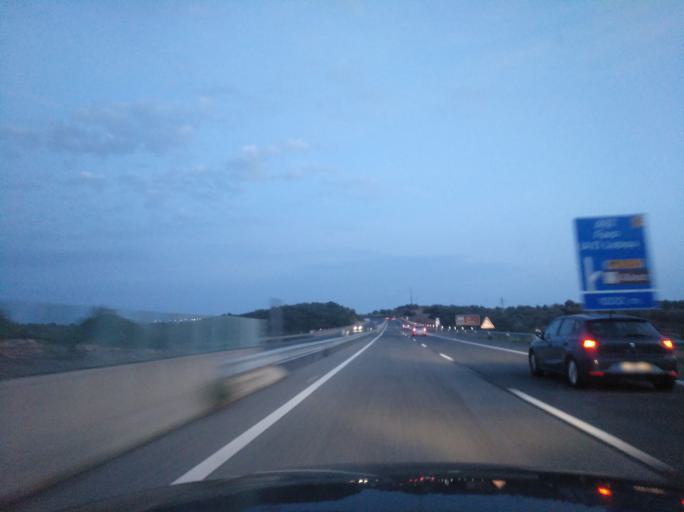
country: PT
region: Faro
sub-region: Portimao
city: Alvor
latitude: 37.1788
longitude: -8.5799
